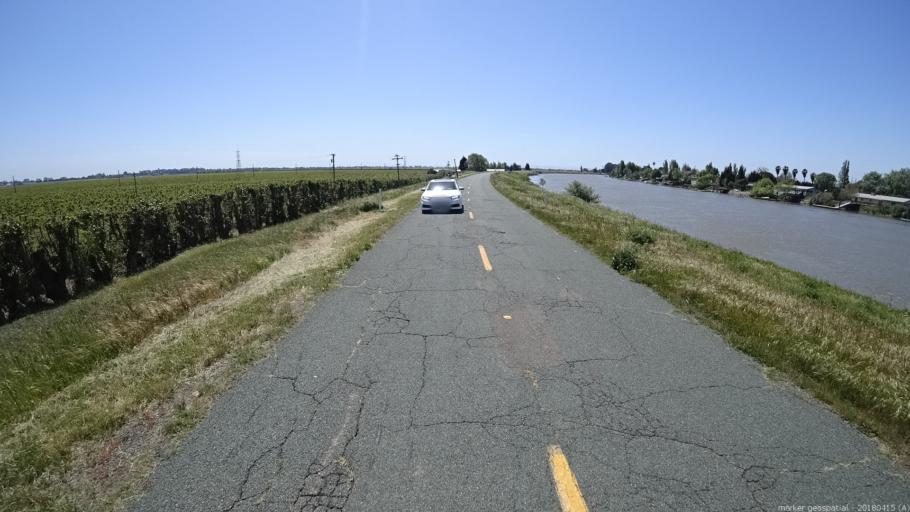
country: US
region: California
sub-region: Solano County
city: Rio Vista
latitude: 38.2022
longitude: -121.6102
